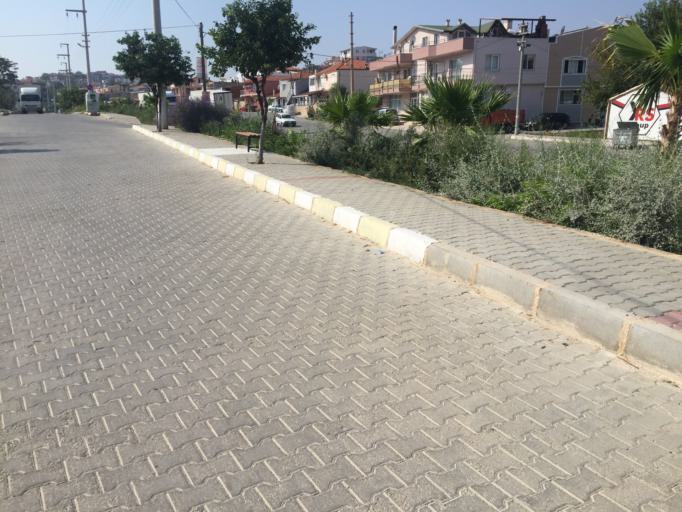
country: TR
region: Izmir
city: Urla
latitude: 38.3272
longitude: 26.7643
